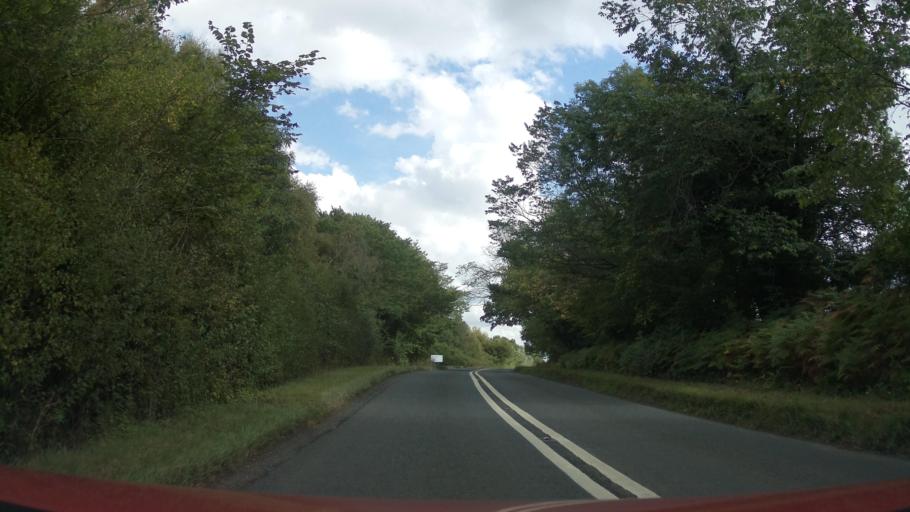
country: GB
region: England
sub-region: North Yorkshire
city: Bedale
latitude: 54.2373
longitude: -1.6770
